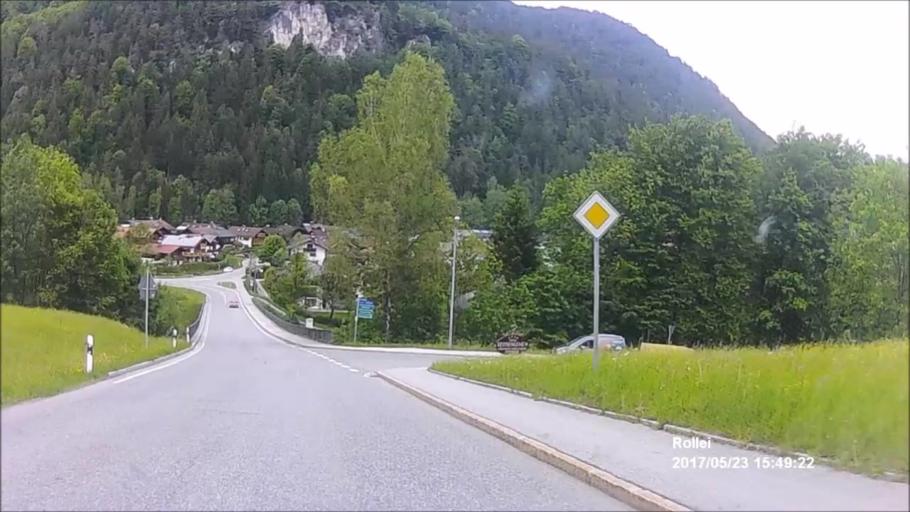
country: DE
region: Bavaria
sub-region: Upper Bavaria
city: Bischofswiesen
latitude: 47.6529
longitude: 12.9579
